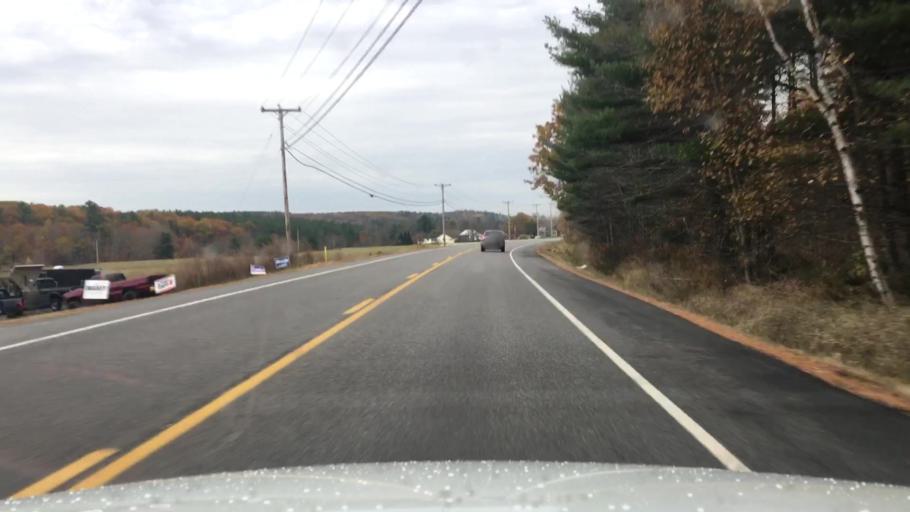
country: US
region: Maine
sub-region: Kennebec County
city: Pittston
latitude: 44.2044
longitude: -69.7537
